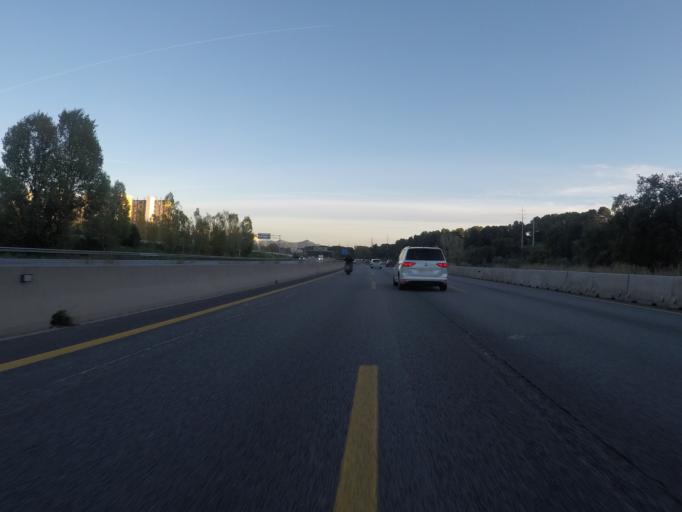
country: ES
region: Catalonia
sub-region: Provincia de Barcelona
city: Barbera del Valles
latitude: 41.5080
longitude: 2.1069
